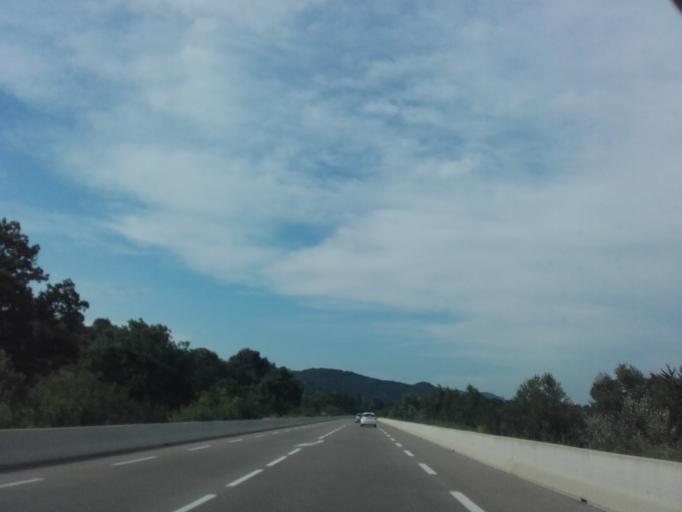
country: FR
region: Rhone-Alpes
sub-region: Departement de l'Ardeche
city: Rochemaure
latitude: 44.5696
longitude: 4.6973
